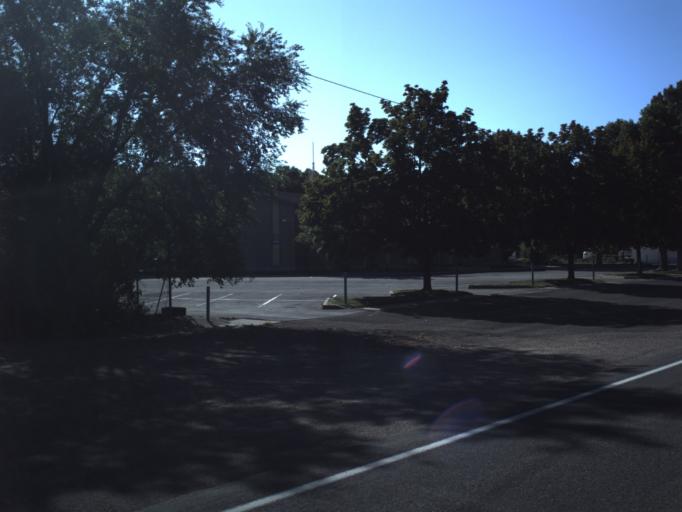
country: US
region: Utah
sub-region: Millard County
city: Delta
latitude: 39.3762
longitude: -112.3361
